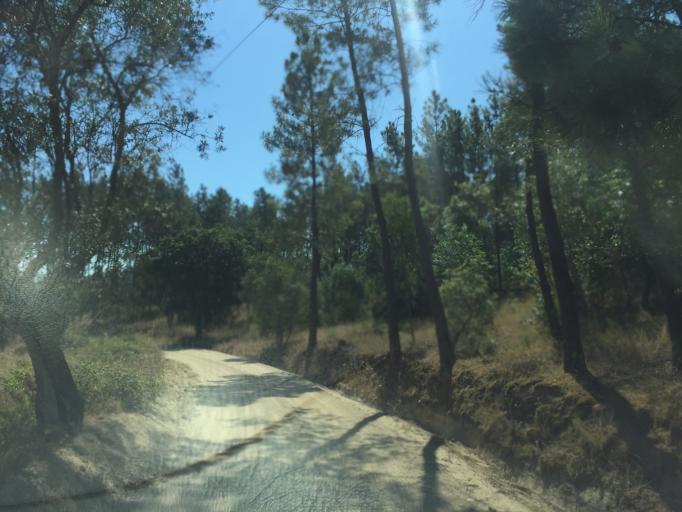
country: PT
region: Santarem
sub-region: Constancia
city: Constancia
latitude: 39.5387
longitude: -8.2930
